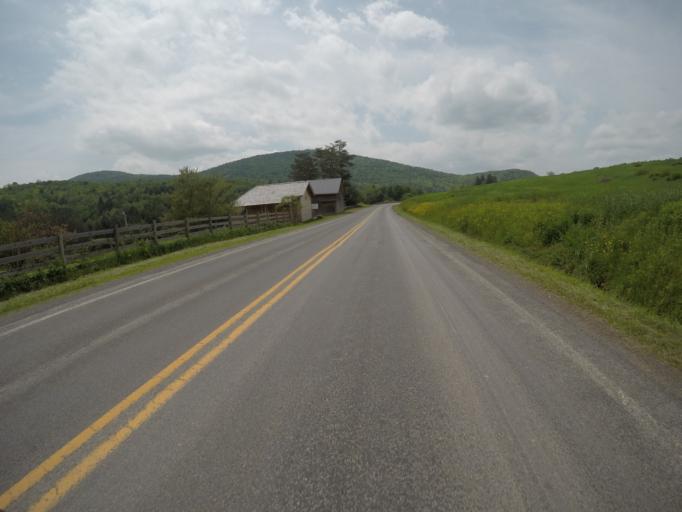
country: US
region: New York
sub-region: Delaware County
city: Delhi
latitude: 42.2616
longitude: -74.7644
